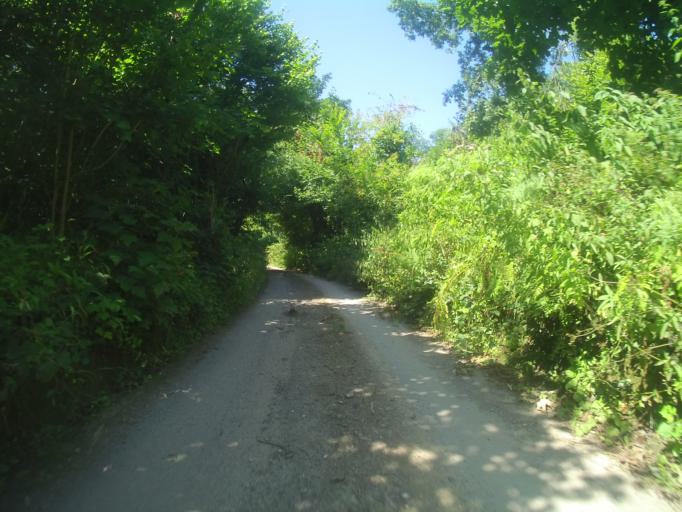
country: GB
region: England
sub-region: Devon
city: Dartmouth
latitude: 50.3569
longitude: -3.6047
